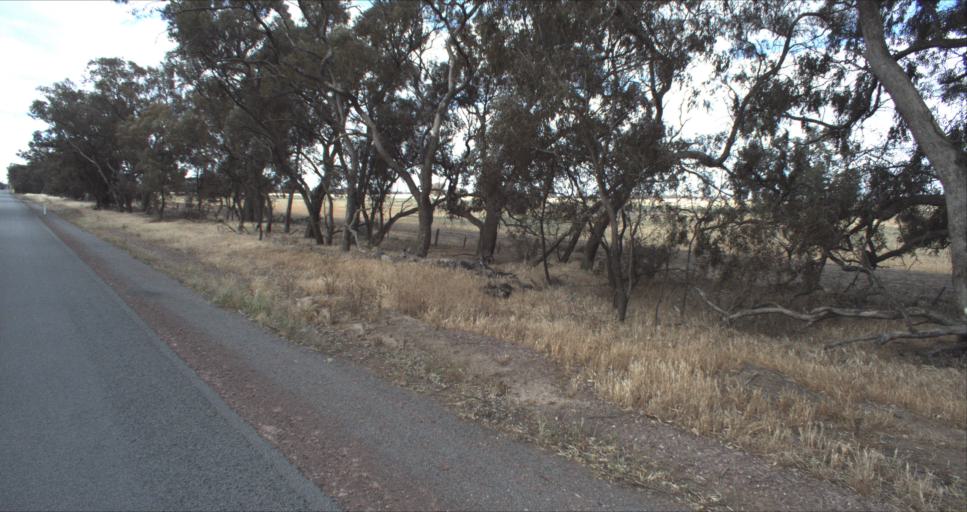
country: AU
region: New South Wales
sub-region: Leeton
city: Leeton
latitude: -34.6813
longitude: 146.3455
